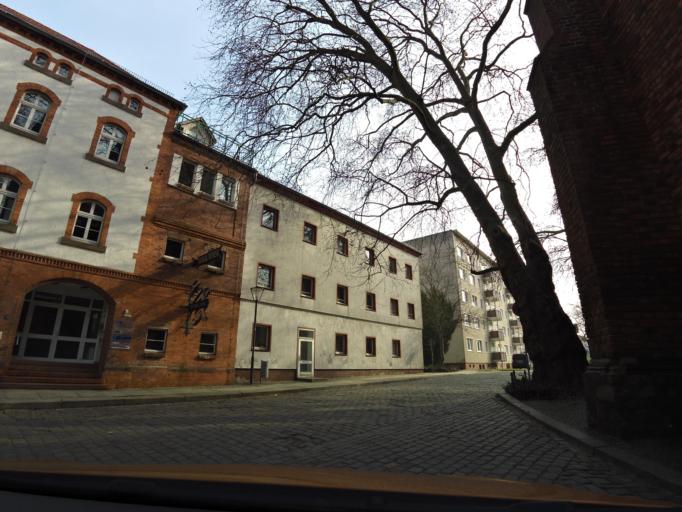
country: DE
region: Brandenburg
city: Frankfurt (Oder)
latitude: 52.3487
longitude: 14.5526
